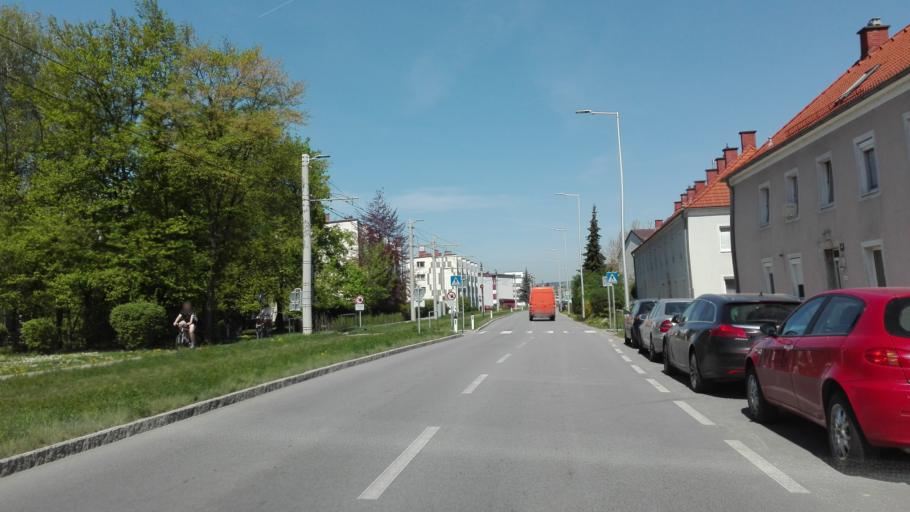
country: AT
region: Upper Austria
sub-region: Politischer Bezirk Linz-Land
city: Traun
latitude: 48.2229
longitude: 14.2358
